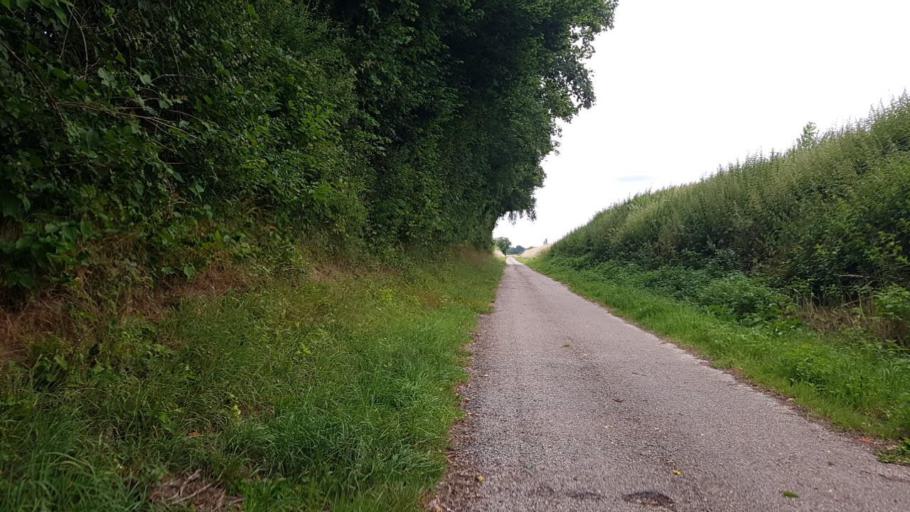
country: FR
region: Picardie
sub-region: Departement de l'Aisne
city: Origny-en-Thierache
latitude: 49.9287
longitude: 3.9935
